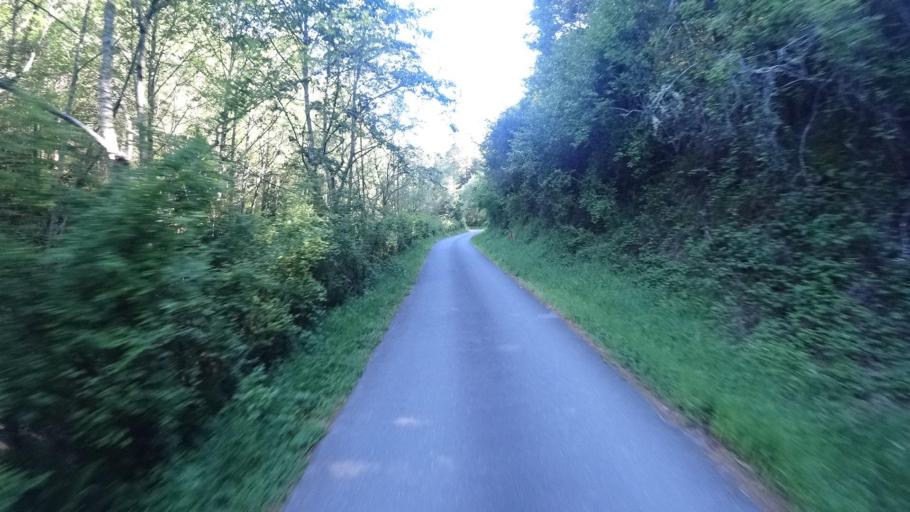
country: US
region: California
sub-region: Humboldt County
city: Ferndale
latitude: 40.5055
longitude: -124.2011
